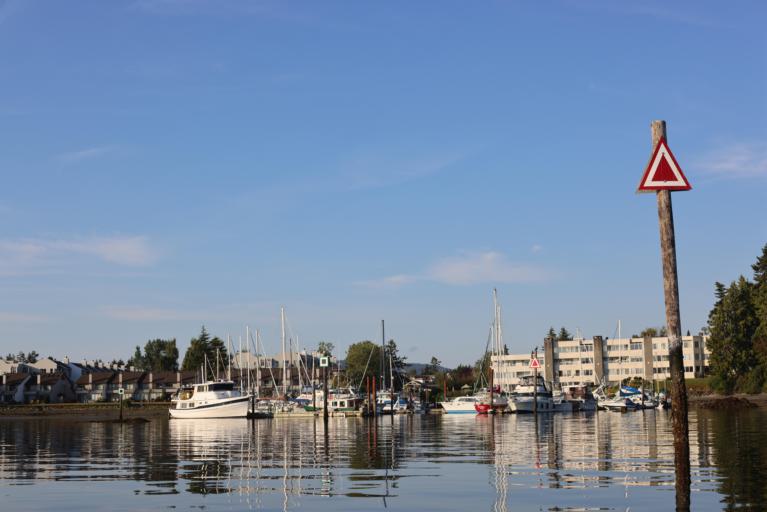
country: CA
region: British Columbia
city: North Saanich
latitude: 48.6705
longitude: -123.4120
